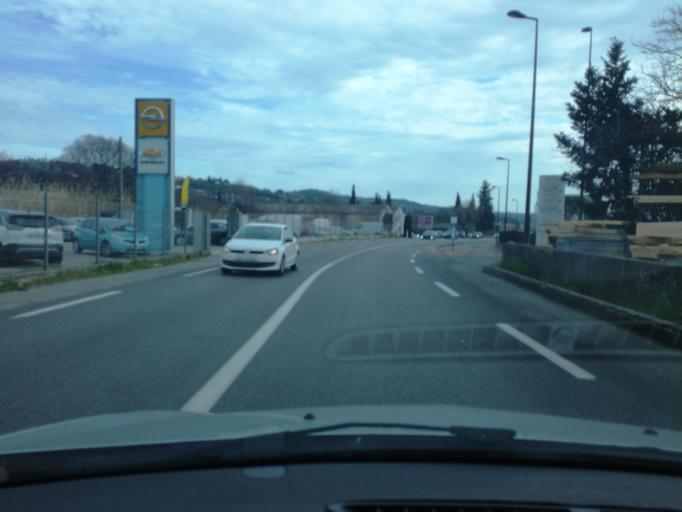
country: FR
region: Provence-Alpes-Cote d'Azur
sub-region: Departement des Alpes-Maritimes
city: Grasse
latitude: 43.6524
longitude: 6.9473
